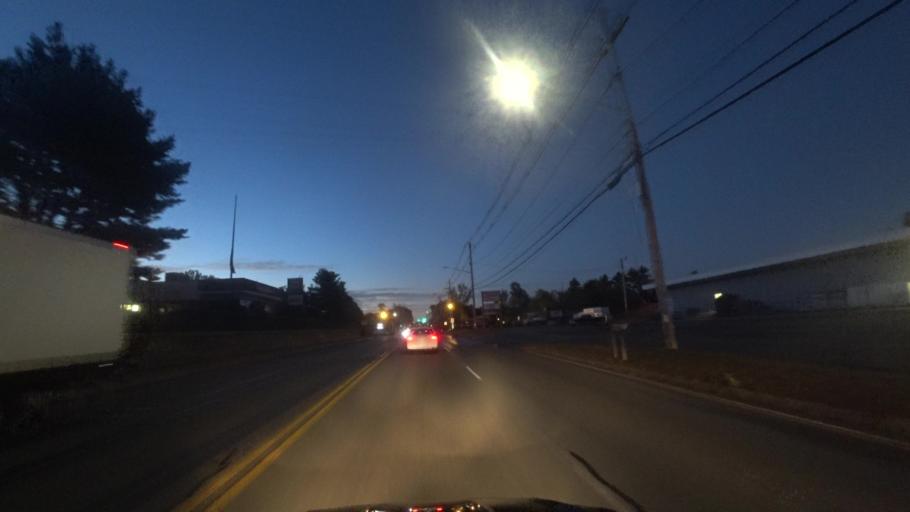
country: US
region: Massachusetts
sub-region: Middlesex County
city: North Reading
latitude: 42.5777
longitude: -71.1114
